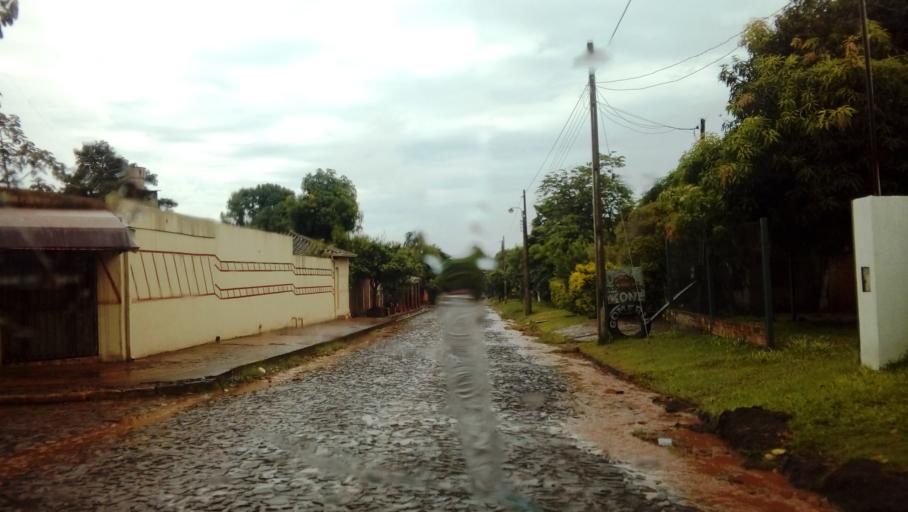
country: PY
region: Alto Parana
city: Ciudad del Este
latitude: -25.4223
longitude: -54.6434
